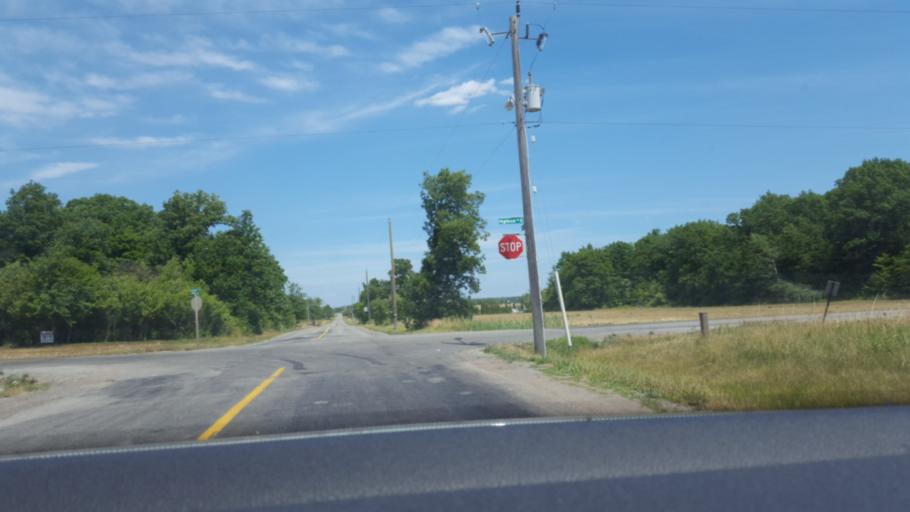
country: CA
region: Ontario
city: Hamilton
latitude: 43.1685
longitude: -79.7237
